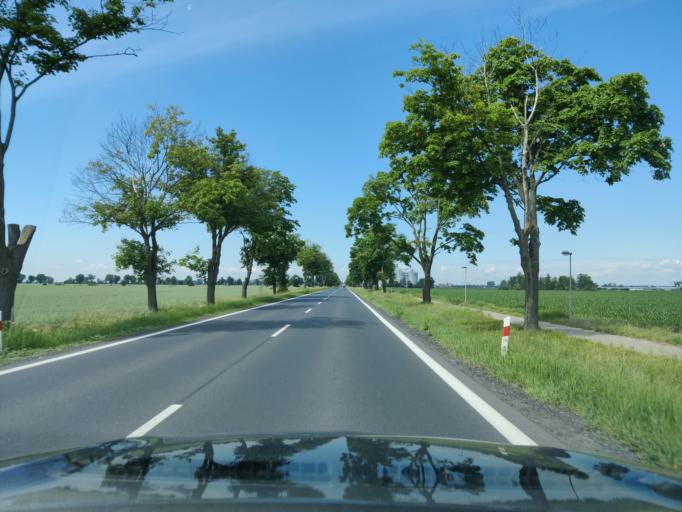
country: PL
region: Greater Poland Voivodeship
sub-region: Powiat grodziski
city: Grodzisk Wielkopolski
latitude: 52.2245
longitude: 16.4141
